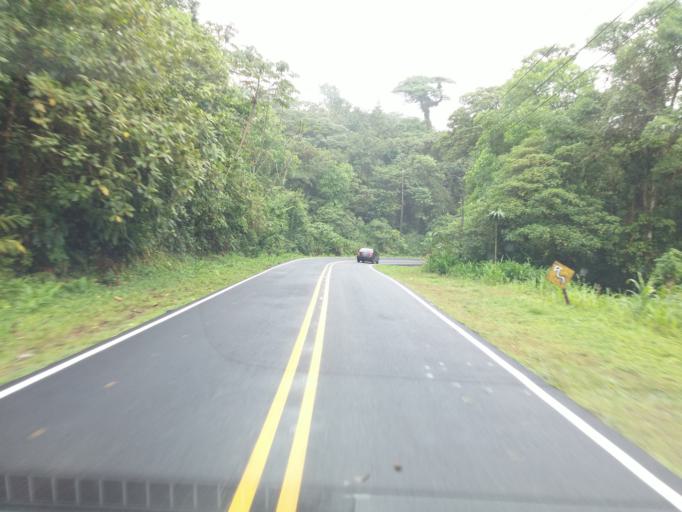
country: CR
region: Alajuela
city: San Ramon
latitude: 10.2036
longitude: -84.5280
